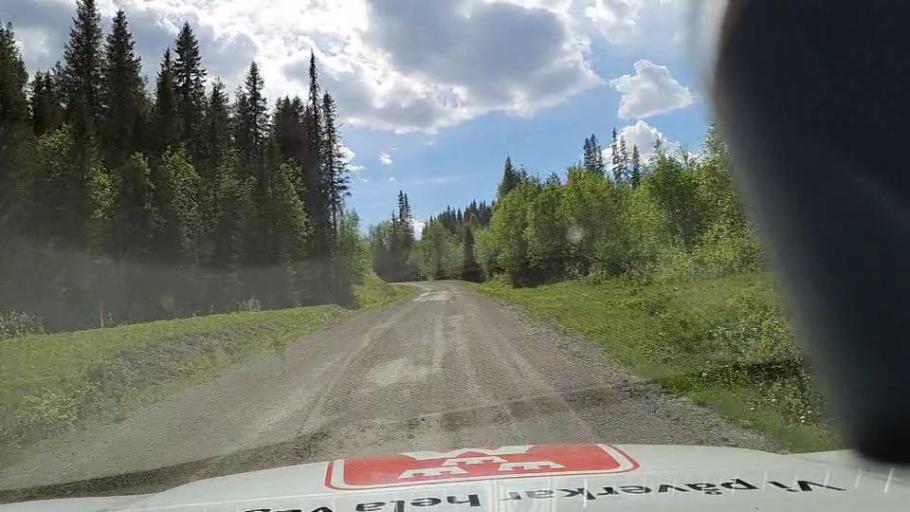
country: SE
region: Vaesterbotten
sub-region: Vilhelmina Kommun
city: Sjoberg
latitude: 64.5641
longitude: 15.8497
